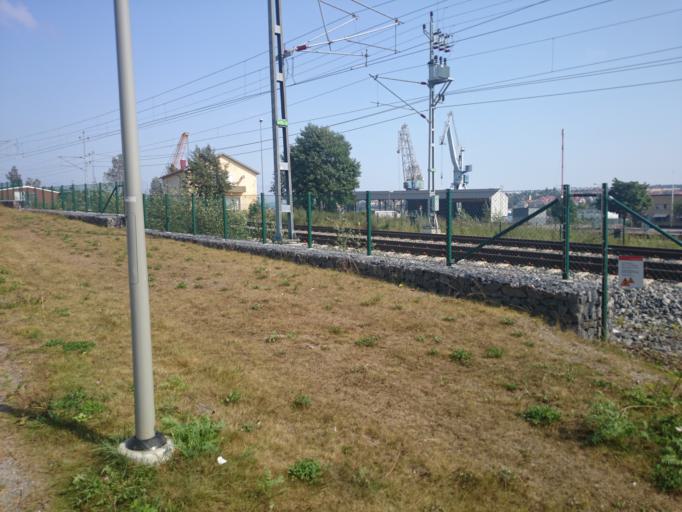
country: SE
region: Vaesternorrland
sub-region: Haernoesands Kommun
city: Haernoesand
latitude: 62.6382
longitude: 17.9316
